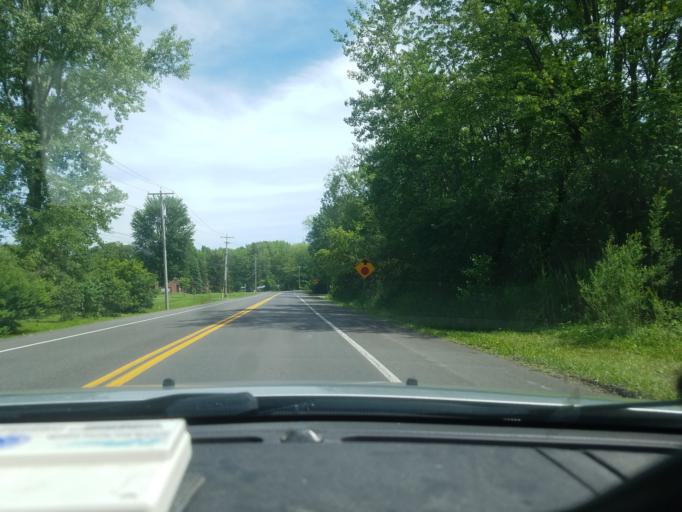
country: US
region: New York
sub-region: Onondaga County
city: East Syracuse
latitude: 43.0777
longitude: -76.0668
